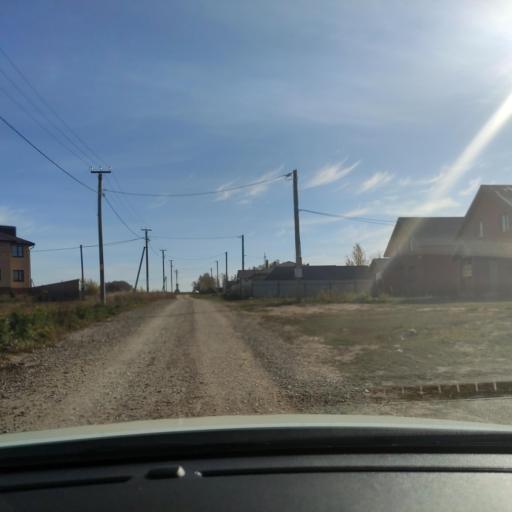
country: RU
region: Tatarstan
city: Vysokaya Gora
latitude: 55.7474
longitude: 49.4081
